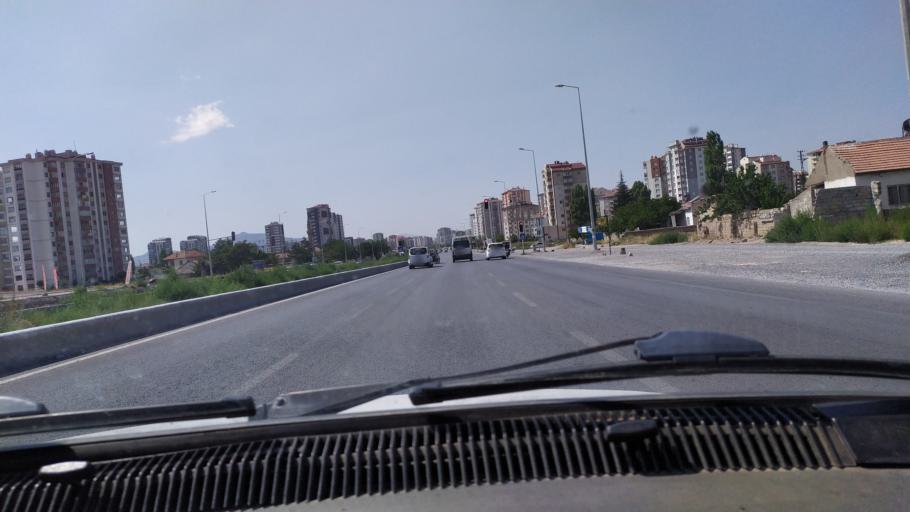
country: TR
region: Kayseri
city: Talas
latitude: 38.7210
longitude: 35.5401
